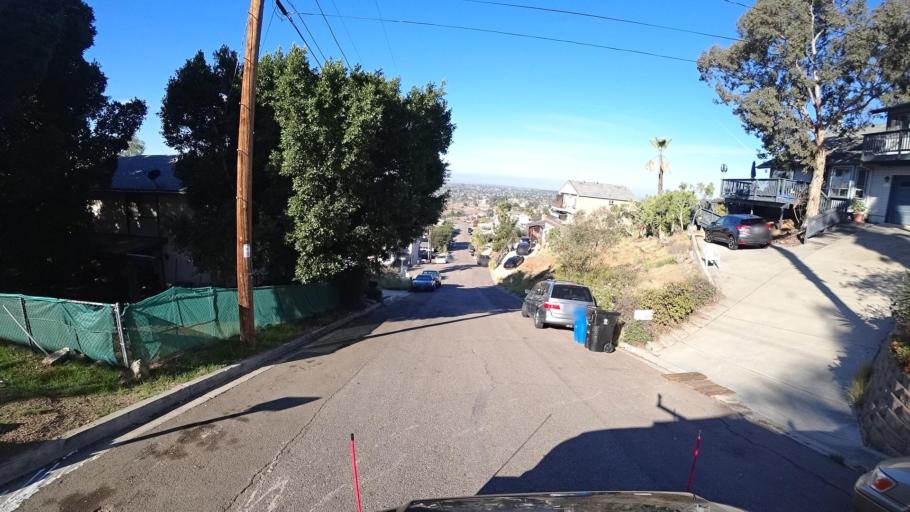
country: US
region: California
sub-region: San Diego County
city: La Presa
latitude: 32.7220
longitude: -116.9946
